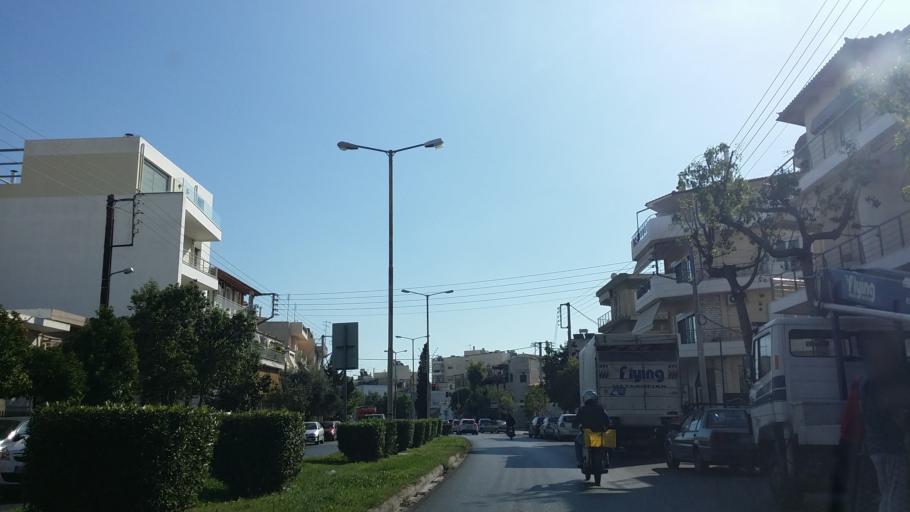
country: GR
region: Attica
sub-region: Nomarchia Athinas
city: Ilion
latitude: 38.0202
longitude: 23.7085
